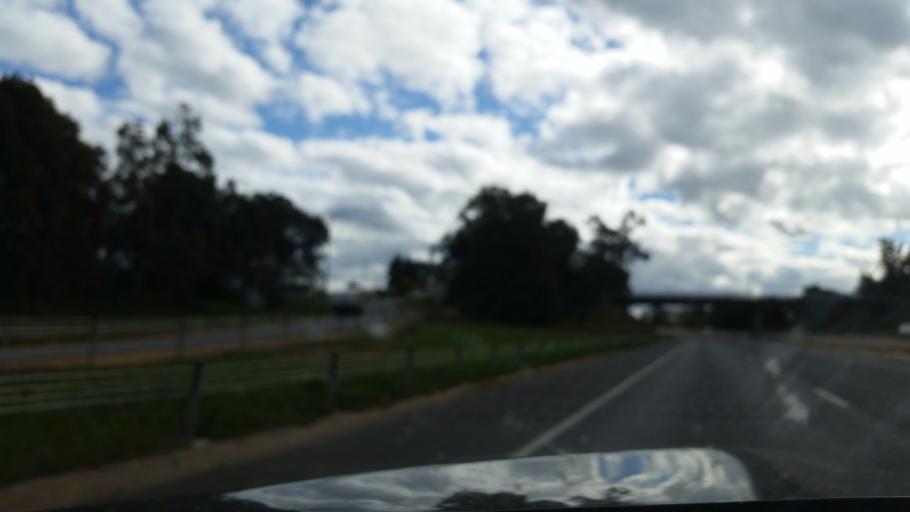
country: AU
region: Victoria
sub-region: Wodonga
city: Wodonga
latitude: -36.1077
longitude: 146.8723
